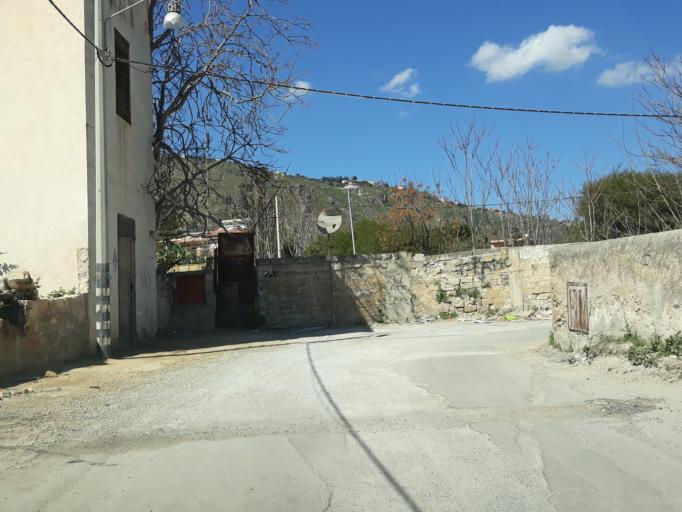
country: IT
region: Sicily
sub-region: Palermo
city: Villa Ciambra
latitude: 38.0905
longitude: 13.3211
